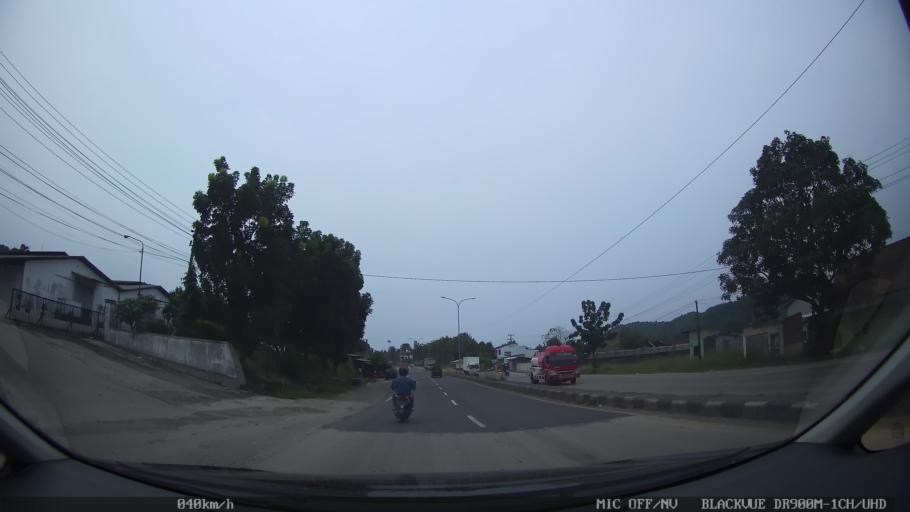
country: ID
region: Lampung
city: Bandarlampung
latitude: -5.4191
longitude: 105.2955
